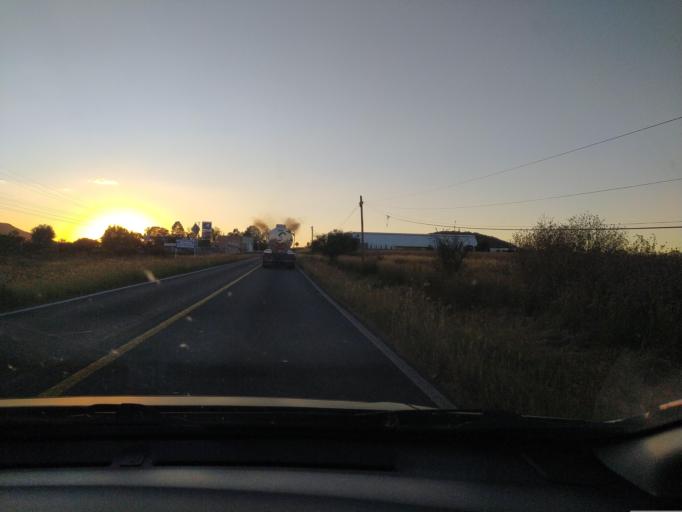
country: MX
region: Jalisco
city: San Miguel el Alto
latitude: 21.0256
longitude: -102.4198
